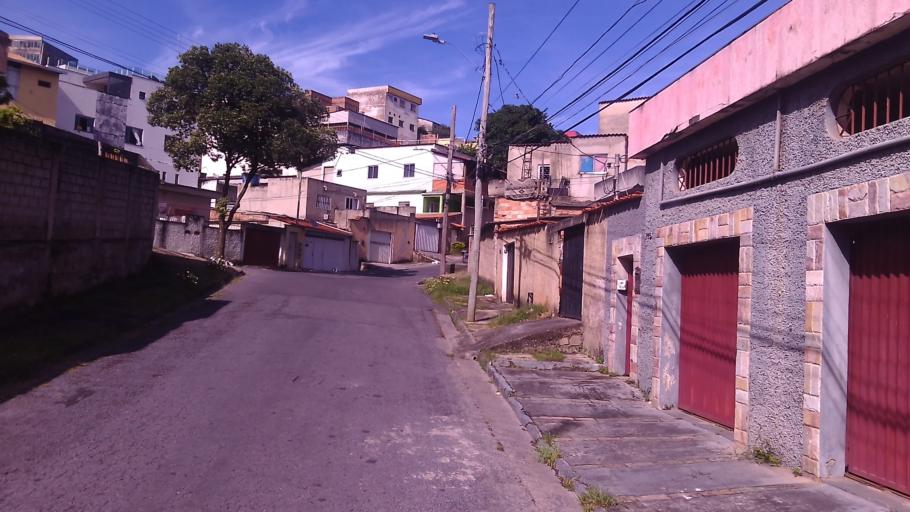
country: BR
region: Minas Gerais
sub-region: Contagem
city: Contagem
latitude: -19.9034
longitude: -44.0121
